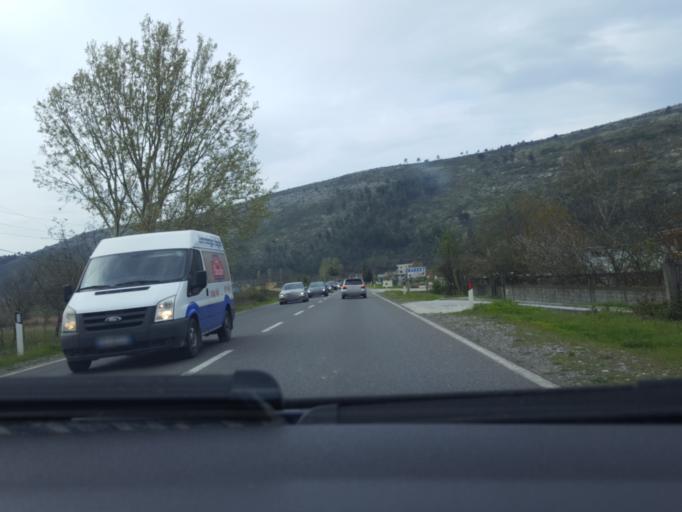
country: AL
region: Lezhe
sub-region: Rrethi i Lezhes
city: Balldreni i Ri
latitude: 41.8067
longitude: 19.6329
